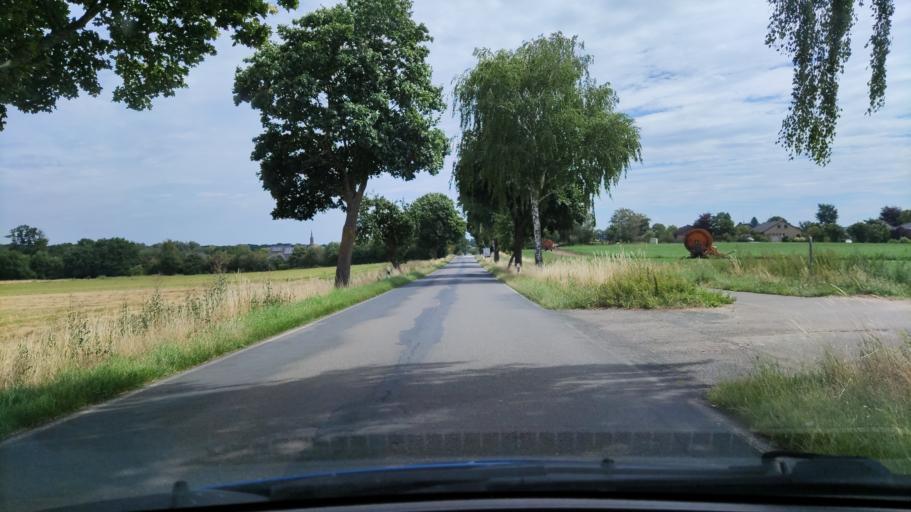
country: DE
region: Lower Saxony
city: Clenze
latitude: 52.9312
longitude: 10.9415
